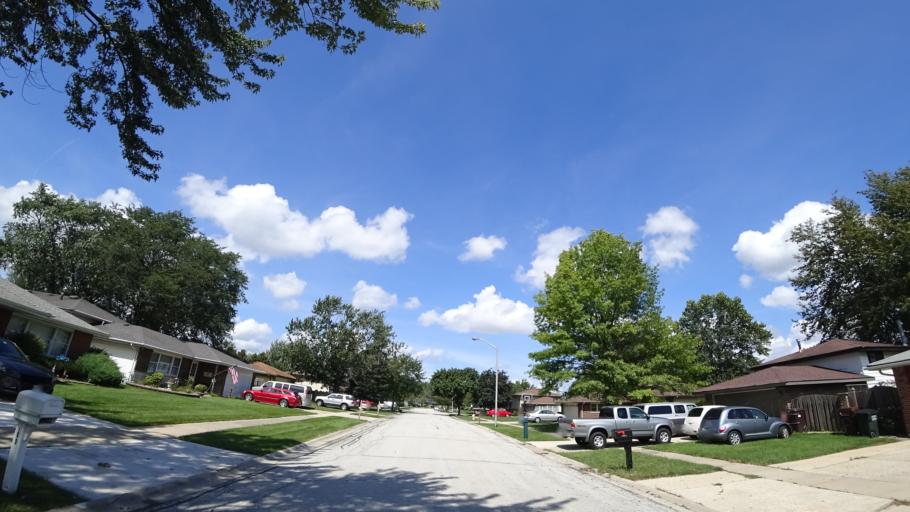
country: US
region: Illinois
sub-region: Cook County
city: Tinley Park
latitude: 41.5634
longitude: -87.7776
